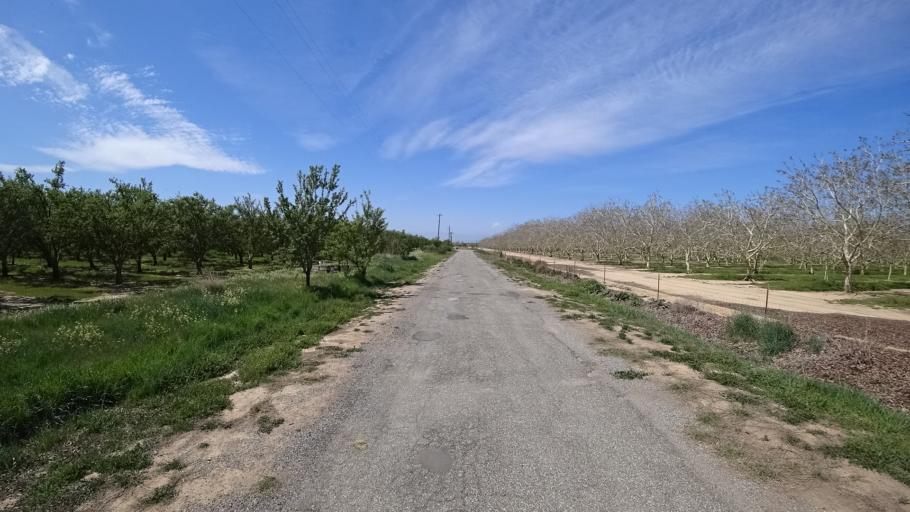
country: US
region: California
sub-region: Glenn County
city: Orland
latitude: 39.6388
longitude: -122.1987
